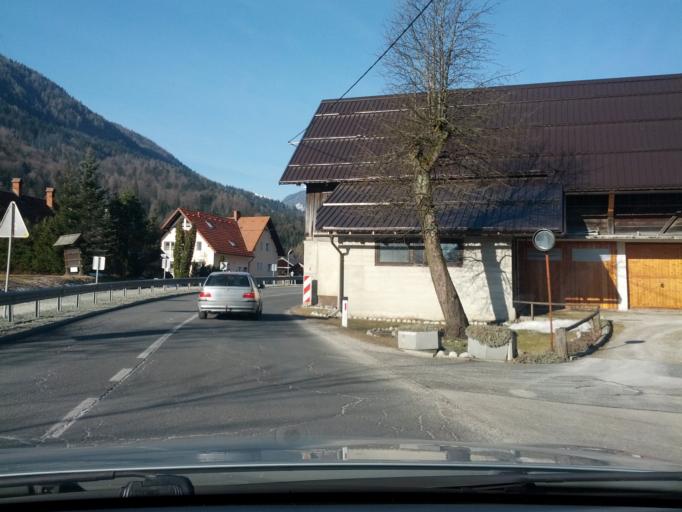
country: SI
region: Kranjska Gora
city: Kranjska Gora
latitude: 46.4844
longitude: 13.8311
